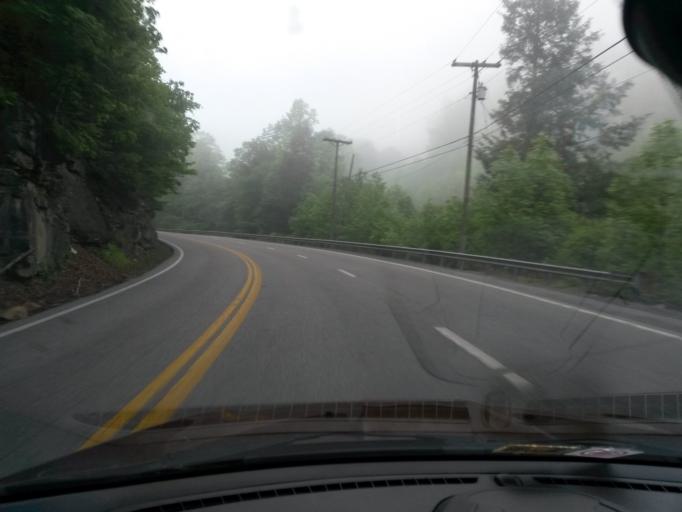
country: US
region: West Virginia
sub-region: McDowell County
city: Welch
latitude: 37.4903
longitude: -81.5399
